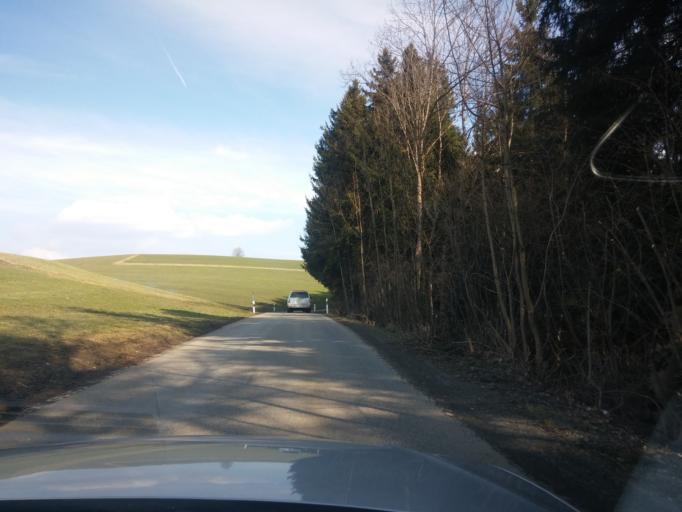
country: DE
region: Bavaria
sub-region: Swabia
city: Durach
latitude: 47.7084
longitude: 10.3672
